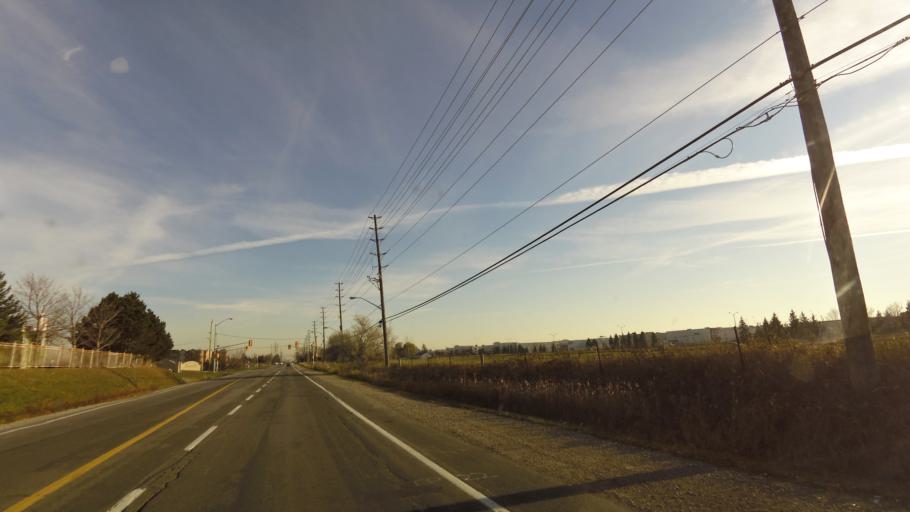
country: CA
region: Ontario
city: Brampton
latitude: 43.7596
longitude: -79.6931
